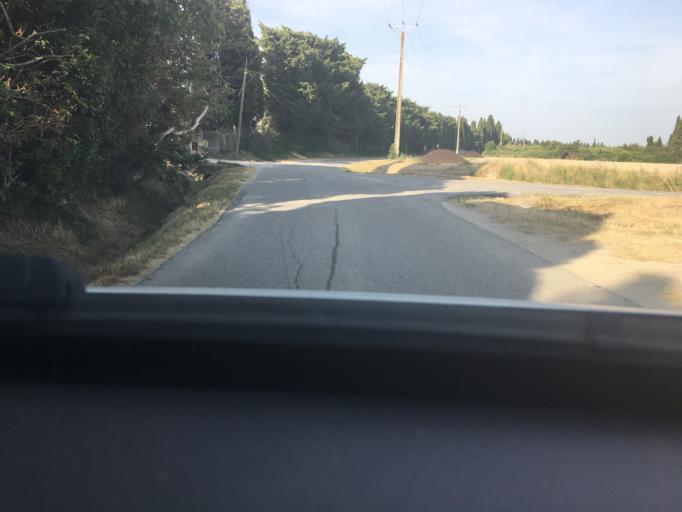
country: FR
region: Provence-Alpes-Cote d'Azur
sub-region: Departement des Bouches-du-Rhone
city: Maillane
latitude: 43.8324
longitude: 4.7979
